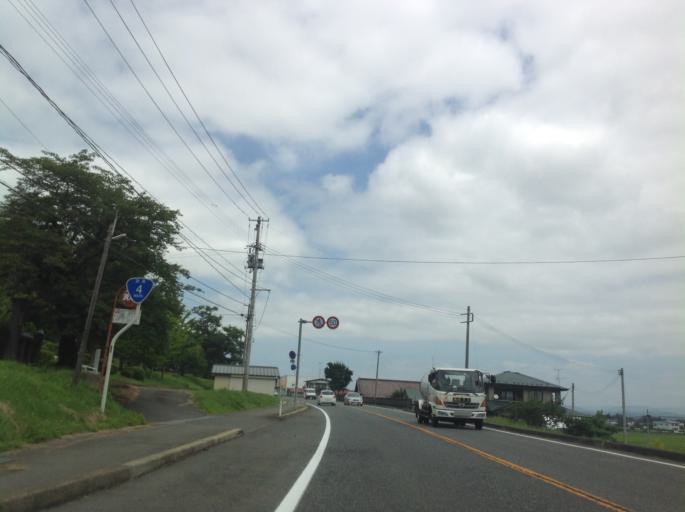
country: JP
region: Iwate
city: Mizusawa
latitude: 39.1095
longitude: 141.1419
